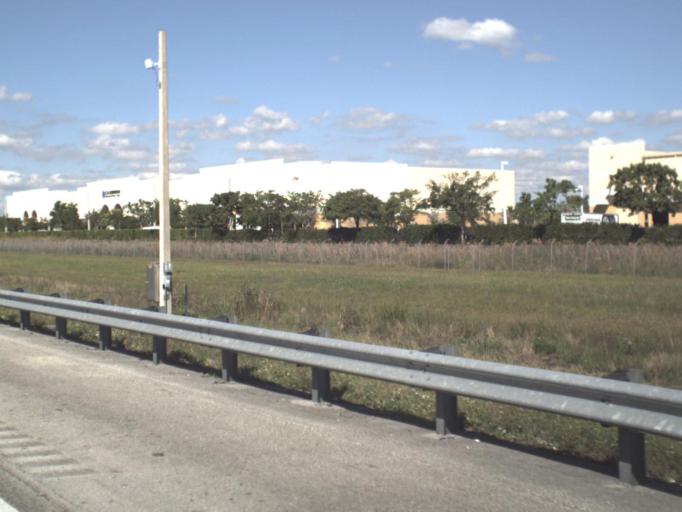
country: US
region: Florida
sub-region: Miami-Dade County
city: Country Club
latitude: 25.9709
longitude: -80.3027
